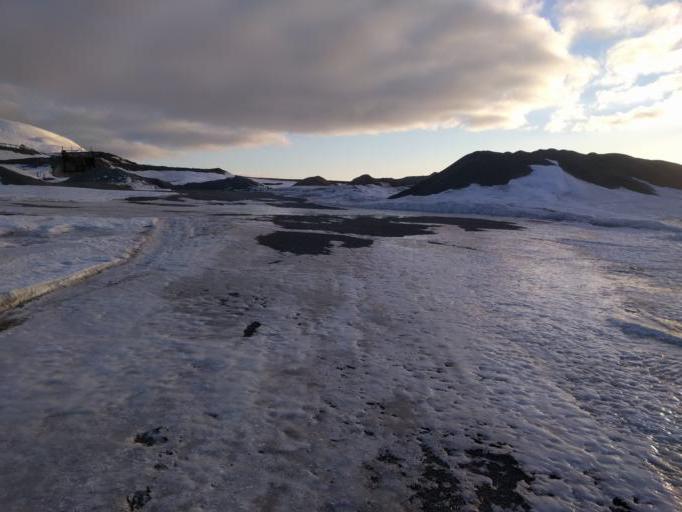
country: SJ
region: Svalbard
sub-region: Spitsbergen
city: Longyearbyen
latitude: 78.2403
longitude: 15.5138
